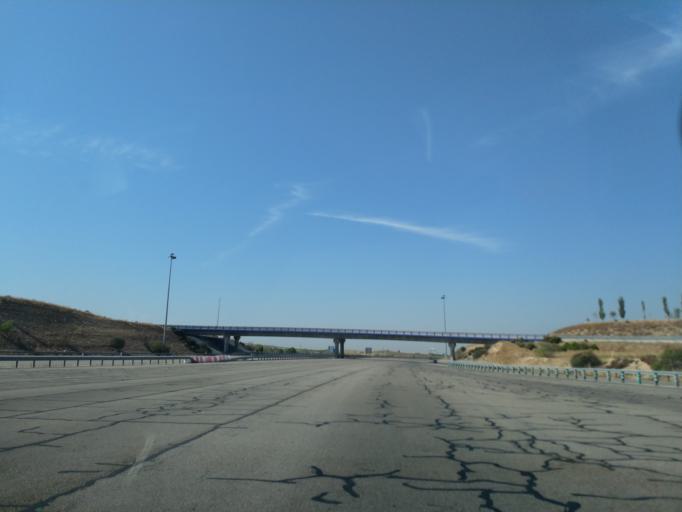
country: ES
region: Madrid
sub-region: Provincia de Madrid
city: Arroyomolinos
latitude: 40.2575
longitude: -3.9107
